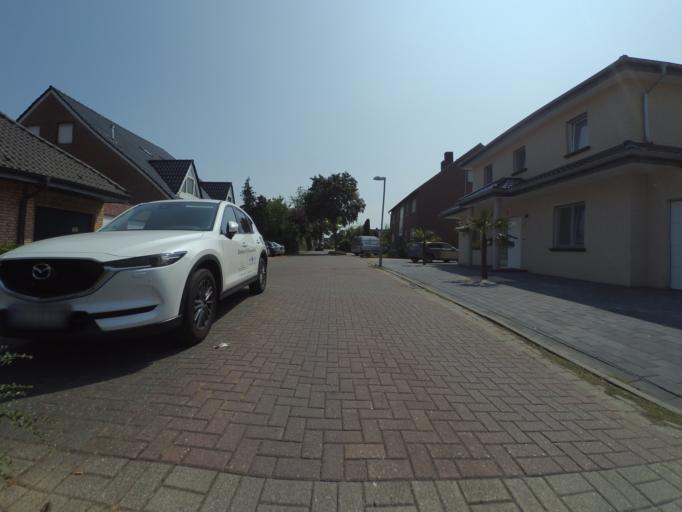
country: DE
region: North Rhine-Westphalia
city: Rees
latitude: 51.7737
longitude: 6.4056
